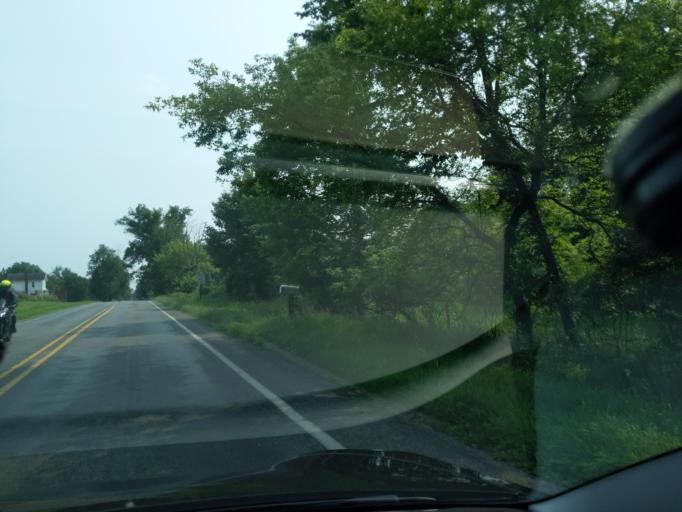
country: US
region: Michigan
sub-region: Eaton County
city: Eaton Rapids
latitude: 42.4742
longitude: -84.5608
